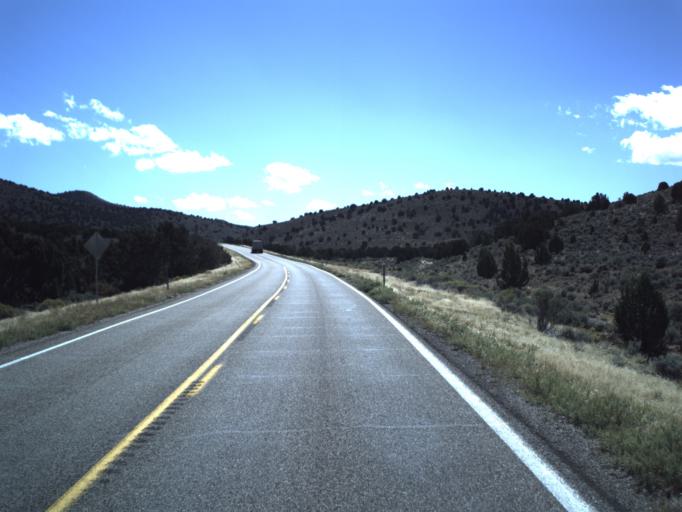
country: US
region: Utah
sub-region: Beaver County
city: Milford
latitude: 38.1299
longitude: -112.9588
